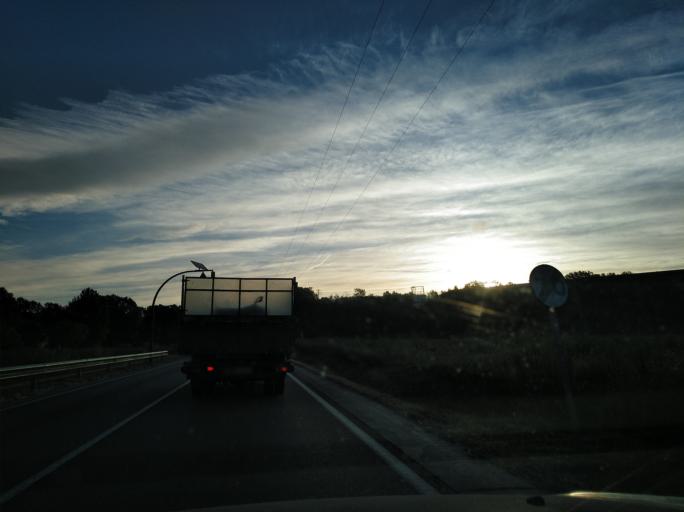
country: ES
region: Catalonia
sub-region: Provincia de Girona
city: Angles
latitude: 41.9587
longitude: 2.6515
